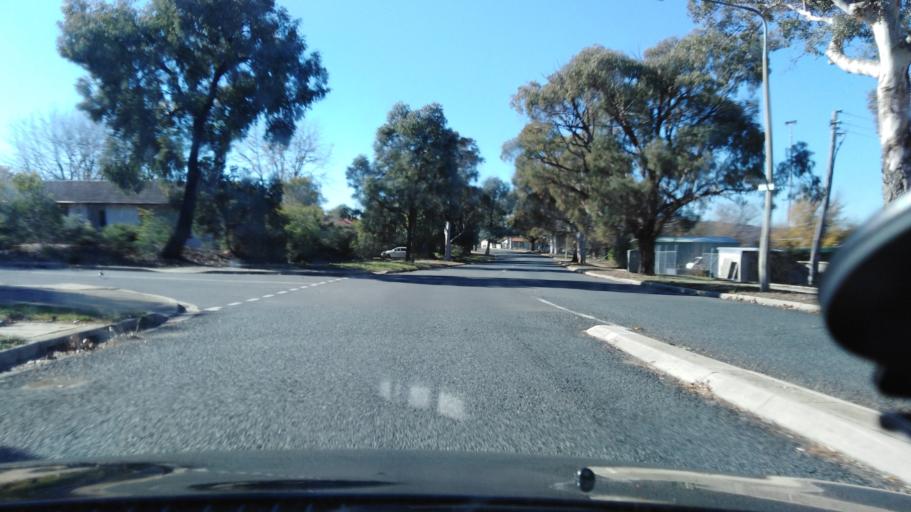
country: AU
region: Australian Capital Territory
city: Forrest
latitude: -35.3463
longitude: 149.0366
